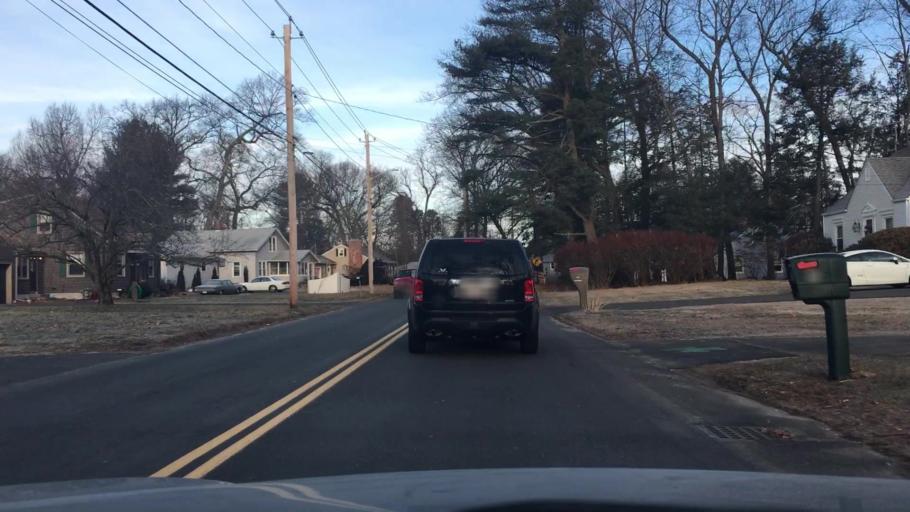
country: US
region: Massachusetts
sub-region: Hampden County
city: Westfield
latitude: 42.1361
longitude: -72.7265
